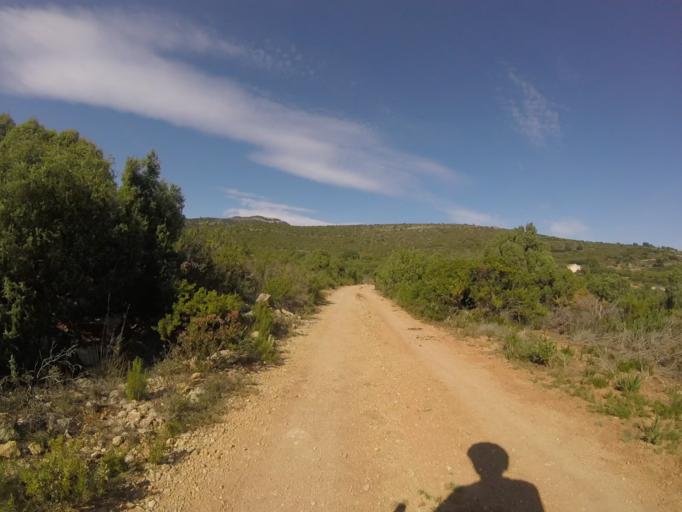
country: ES
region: Valencia
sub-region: Provincia de Castello
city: Sierra-Engarceran
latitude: 40.2722
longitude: 0.0155
